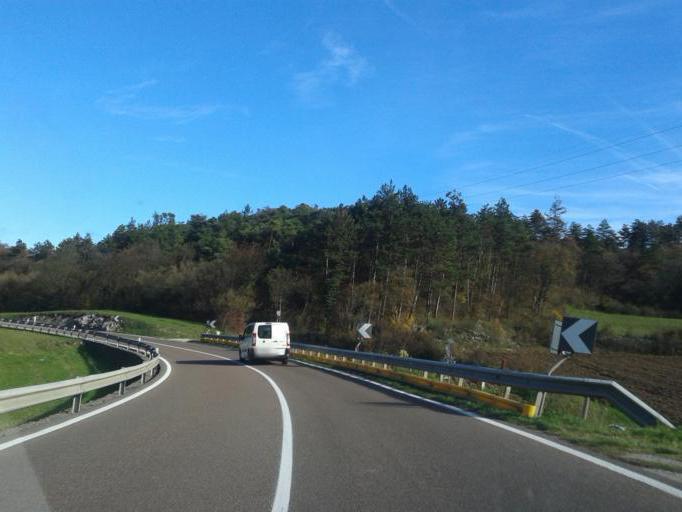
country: IT
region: Trentino-Alto Adige
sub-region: Provincia di Trento
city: Terlago
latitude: 46.0767
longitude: 11.0267
